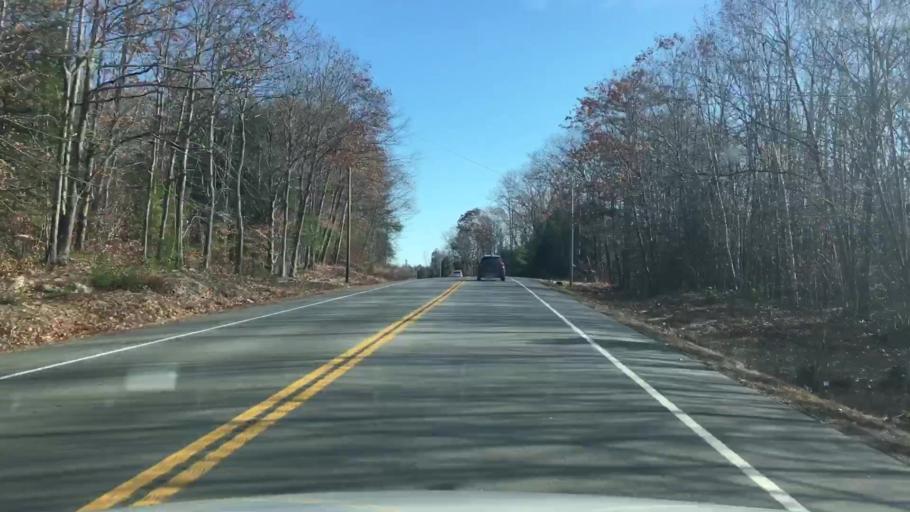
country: US
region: Maine
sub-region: Knox County
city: Washington
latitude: 44.2495
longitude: -69.4055
